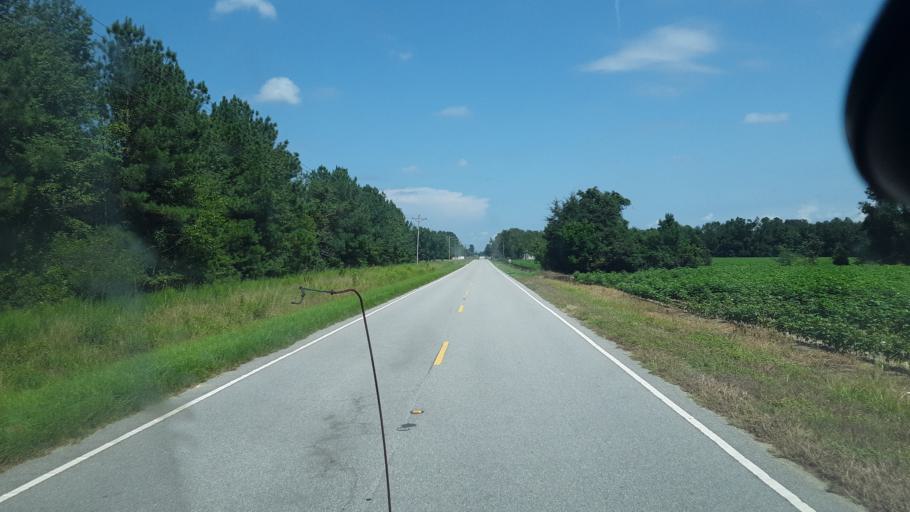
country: US
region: South Carolina
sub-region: Bamberg County
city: Bamberg
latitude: 33.4189
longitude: -81.0190
